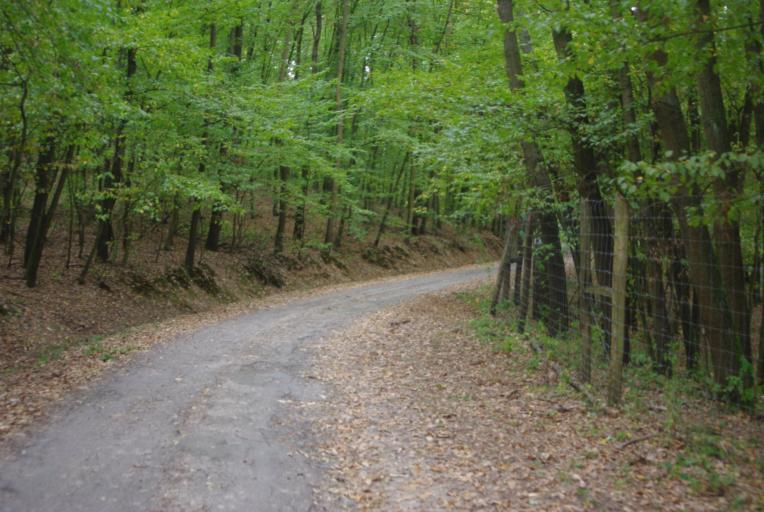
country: HU
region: Pest
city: Nagymaros
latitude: 47.8057
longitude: 18.9249
